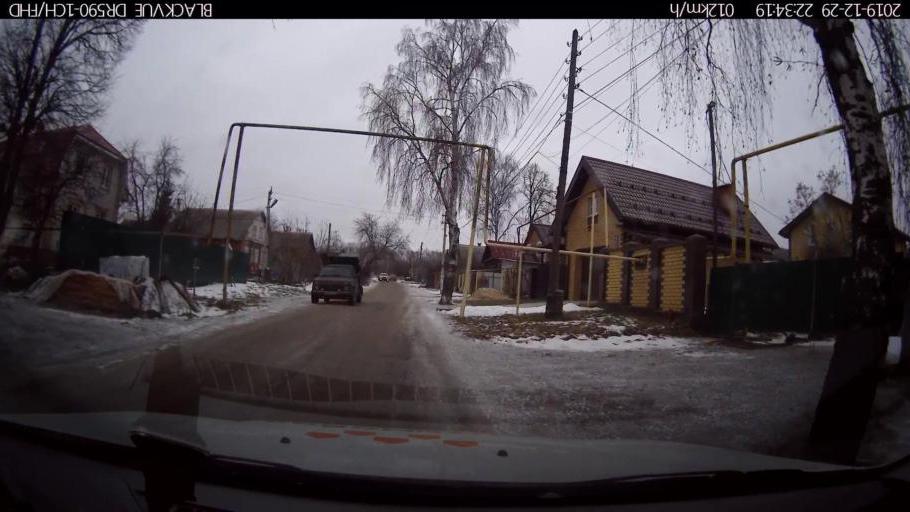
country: RU
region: Nizjnij Novgorod
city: Afonino
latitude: 56.2043
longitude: 43.9861
